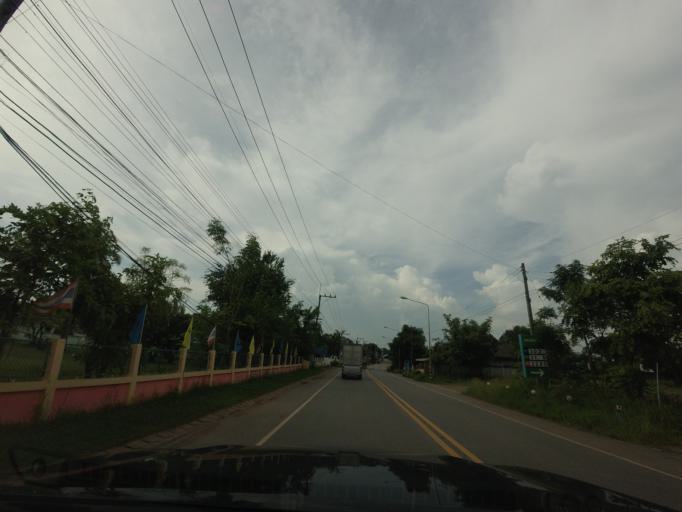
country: TH
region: Changwat Nong Bua Lamphu
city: Suwannakhuha
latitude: 17.4668
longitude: 102.3475
